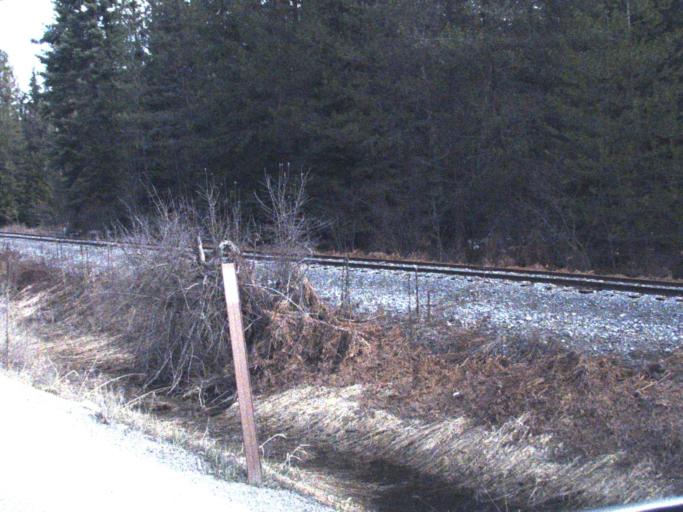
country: US
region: Washington
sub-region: Stevens County
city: Chewelah
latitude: 48.6042
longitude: -117.3631
